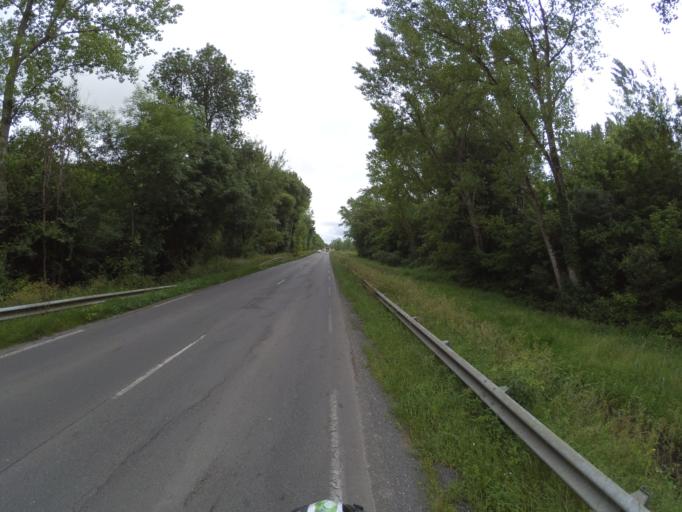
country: FR
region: Aquitaine
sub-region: Departement de la Gironde
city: Soussans
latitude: 45.0656
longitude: -0.7205
